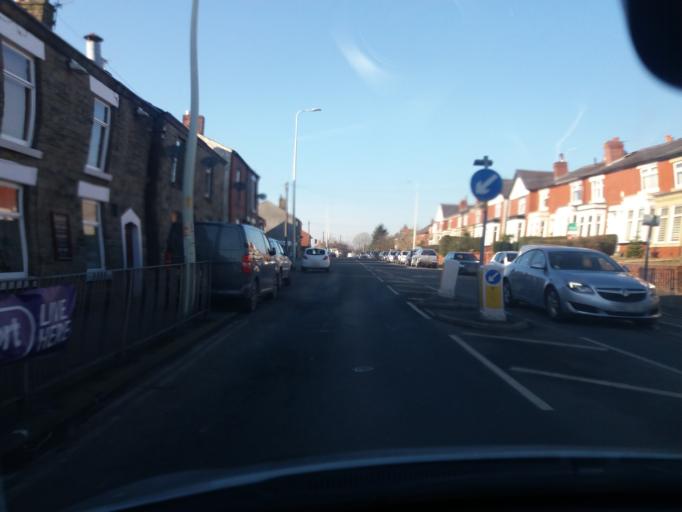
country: GB
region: England
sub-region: Lancashire
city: Adlington
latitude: 53.6226
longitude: -2.6056
